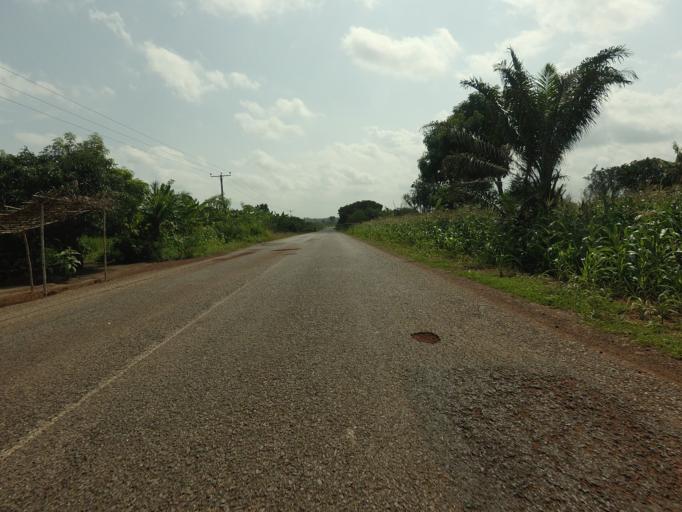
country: TG
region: Maritime
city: Tsevie
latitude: 6.3927
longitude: 0.8165
